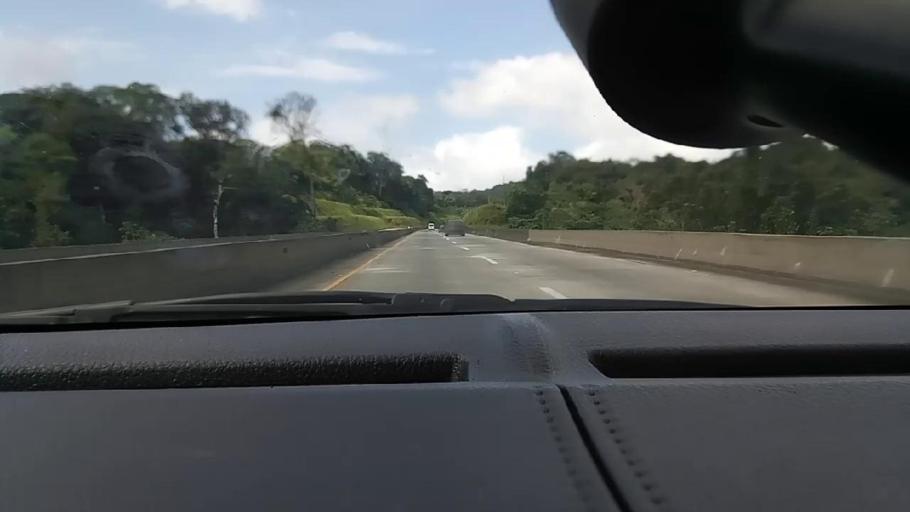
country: PA
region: Colon
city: Gatun
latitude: 9.2824
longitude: -79.7708
